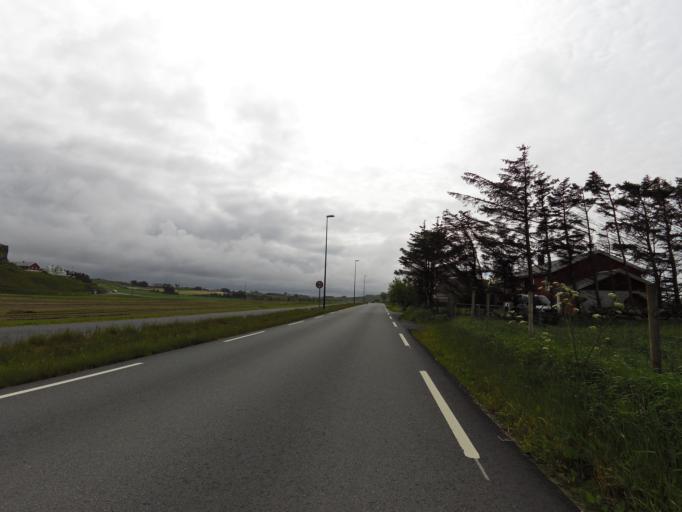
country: NO
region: Rogaland
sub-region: Klepp
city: Kleppe
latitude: 58.8409
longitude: 5.5696
